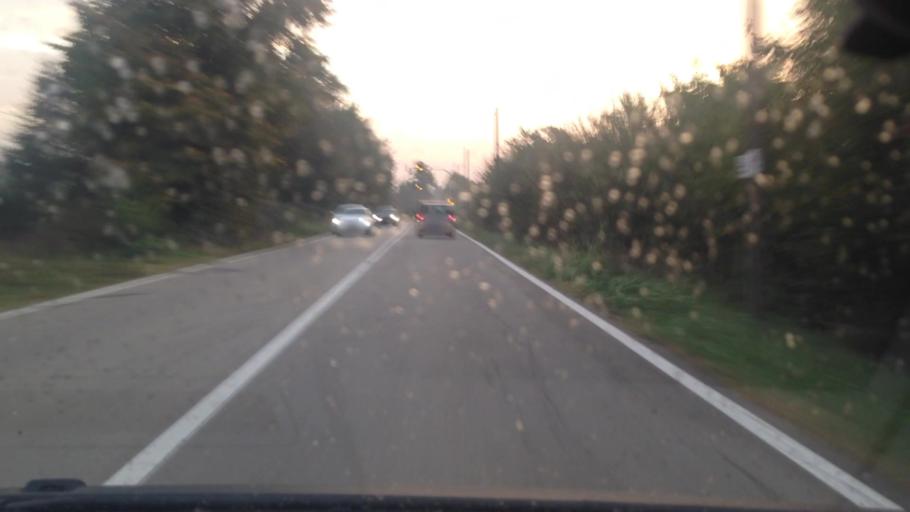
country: IT
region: Piedmont
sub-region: Provincia di Asti
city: Cerro Tanaro
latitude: 44.8890
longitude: 8.3687
